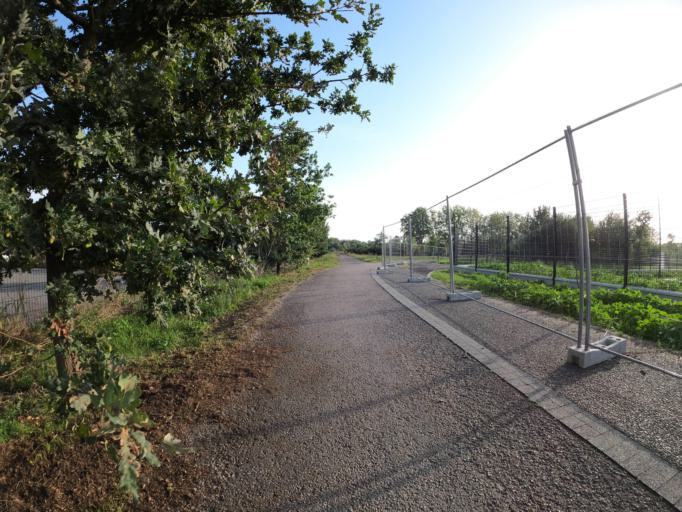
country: FR
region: Midi-Pyrenees
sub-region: Departement de la Haute-Garonne
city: Vieille-Toulouse
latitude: 43.5536
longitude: 1.4312
